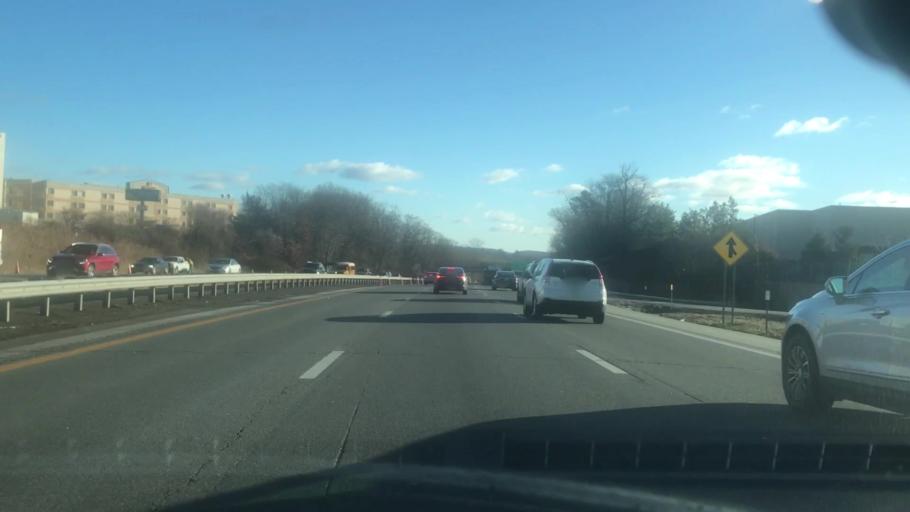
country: US
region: New York
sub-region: Rockland County
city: Nanuet
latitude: 41.1029
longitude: -74.0225
